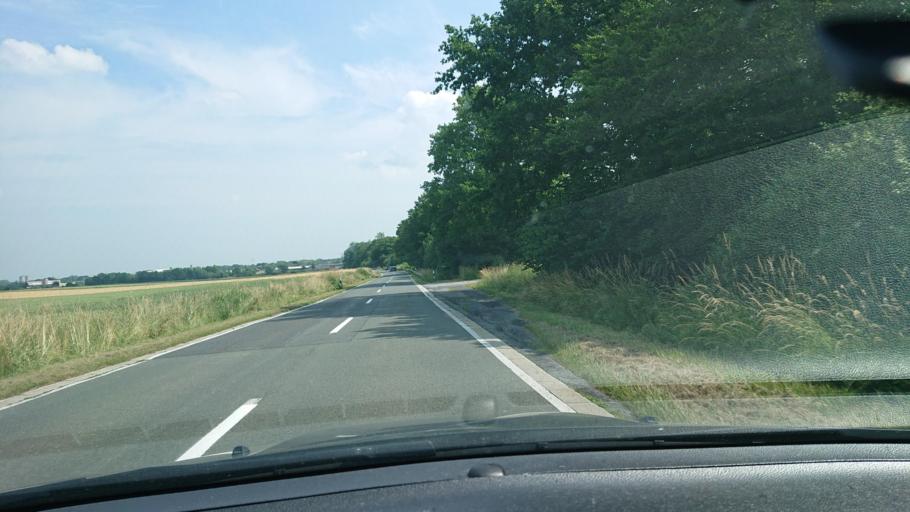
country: DE
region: North Rhine-Westphalia
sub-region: Regierungsbezirk Arnsberg
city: Soest
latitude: 51.5492
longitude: 8.0749
